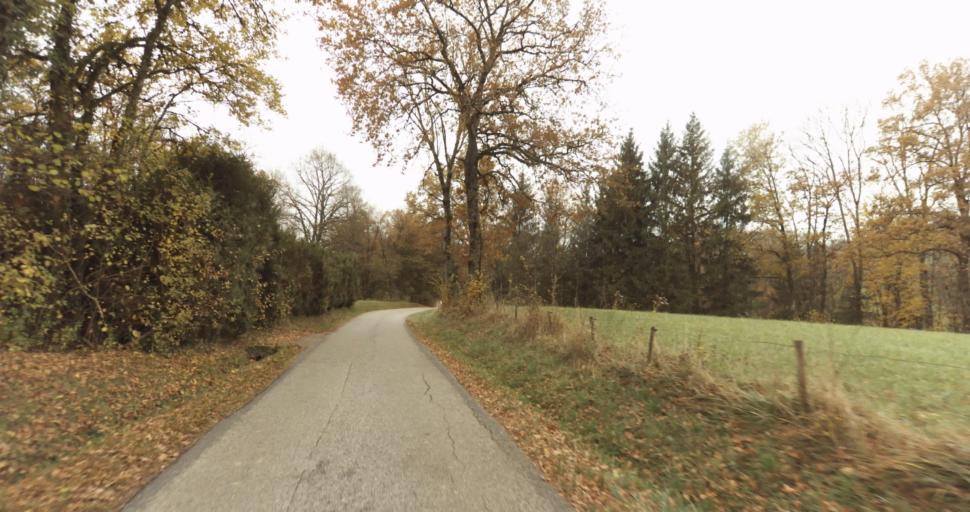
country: FR
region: Rhone-Alpes
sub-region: Departement de la Haute-Savoie
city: Poisy
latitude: 45.9075
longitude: 6.0533
